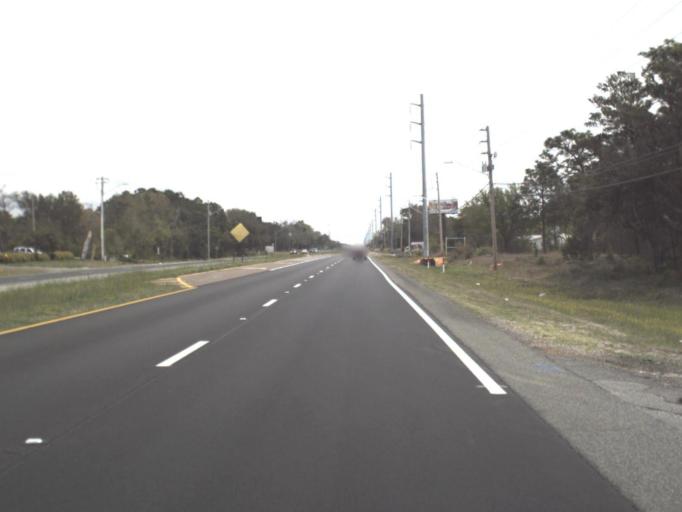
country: US
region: Florida
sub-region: Santa Rosa County
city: Tiger Point
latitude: 30.3947
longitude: -87.0334
